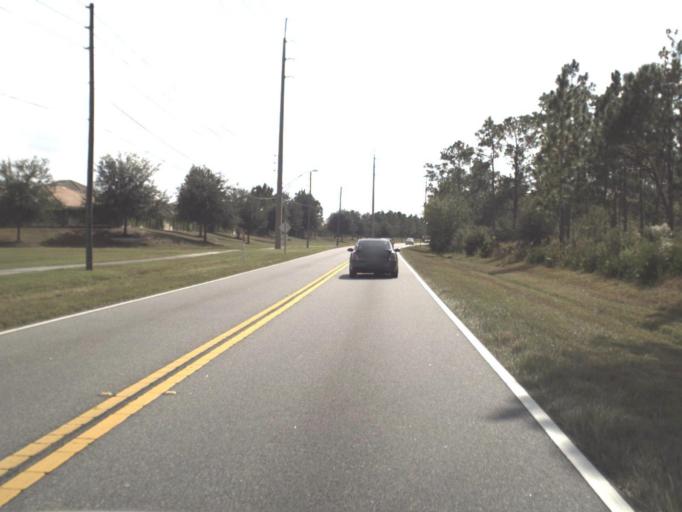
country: US
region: Florida
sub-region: Osceola County
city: Poinciana
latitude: 28.1803
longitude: -81.4547
